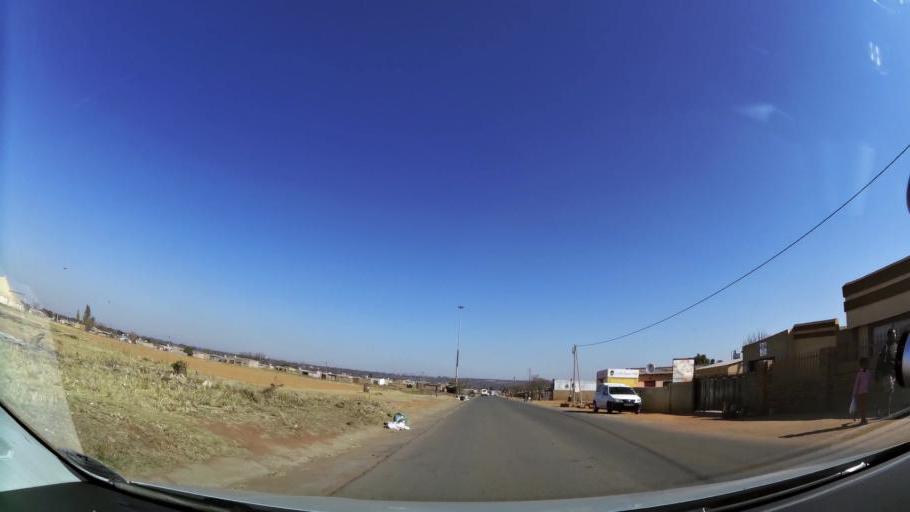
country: ZA
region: Gauteng
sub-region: Ekurhuleni Metropolitan Municipality
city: Tembisa
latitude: -26.0264
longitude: 28.2352
